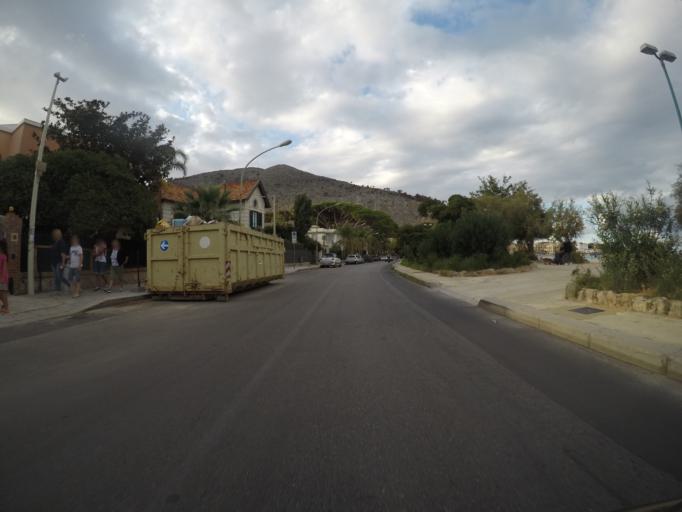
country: IT
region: Sicily
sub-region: Palermo
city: Palermo
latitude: 38.2039
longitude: 13.3253
